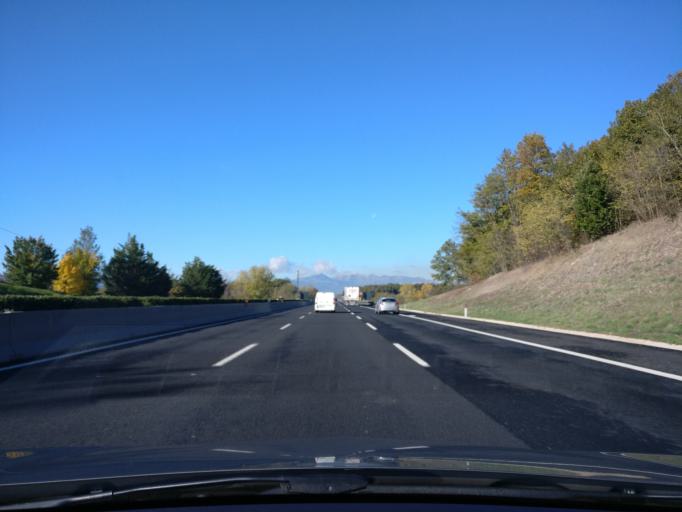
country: IT
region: Latium
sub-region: Provincia di Frosinone
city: Ceprano
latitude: 41.5476
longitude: 13.4719
